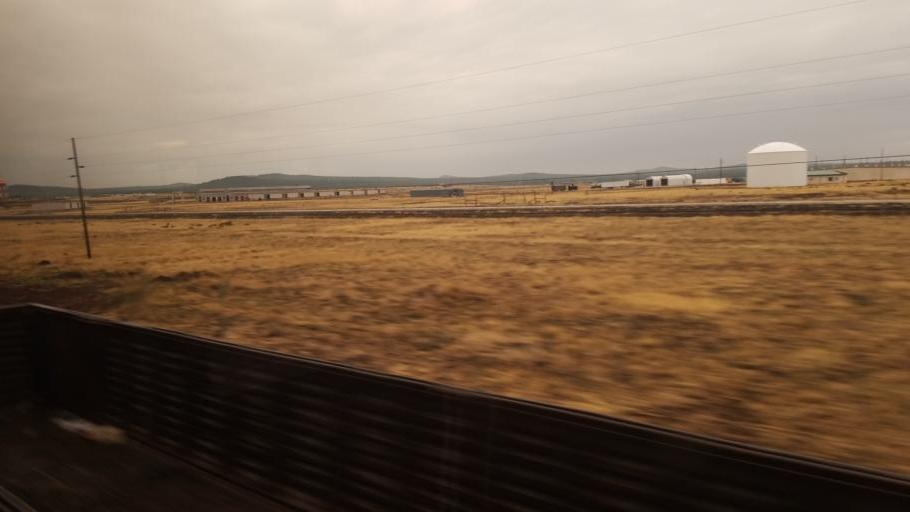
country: US
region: Arizona
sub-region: Coconino County
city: Parks
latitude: 35.2376
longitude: -111.8402
